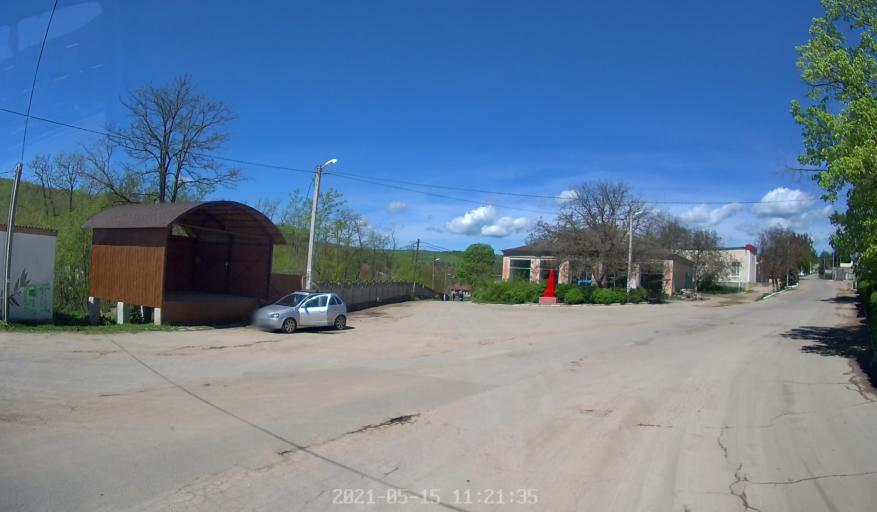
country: MD
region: Hincesti
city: Hincesti
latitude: 46.8241
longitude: 28.6741
